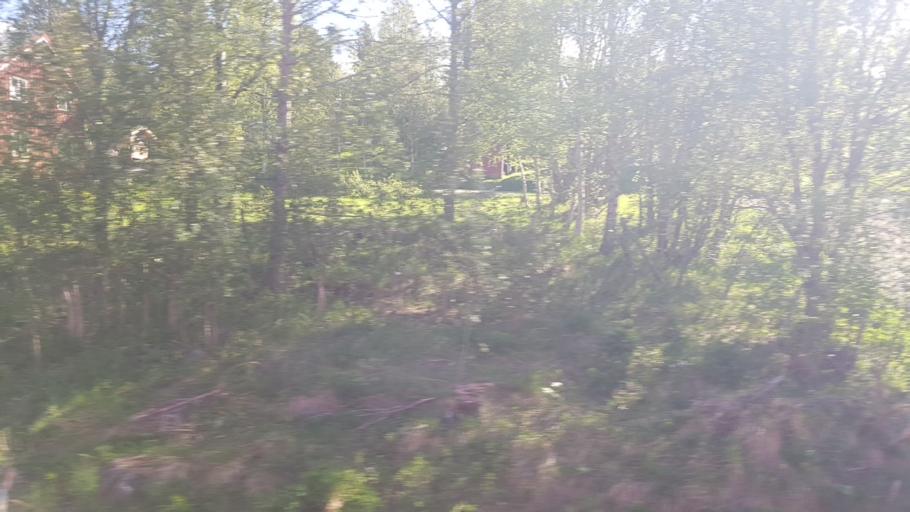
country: NO
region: Sor-Trondelag
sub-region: Rennebu
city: Berkak
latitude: 62.8305
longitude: 10.0130
